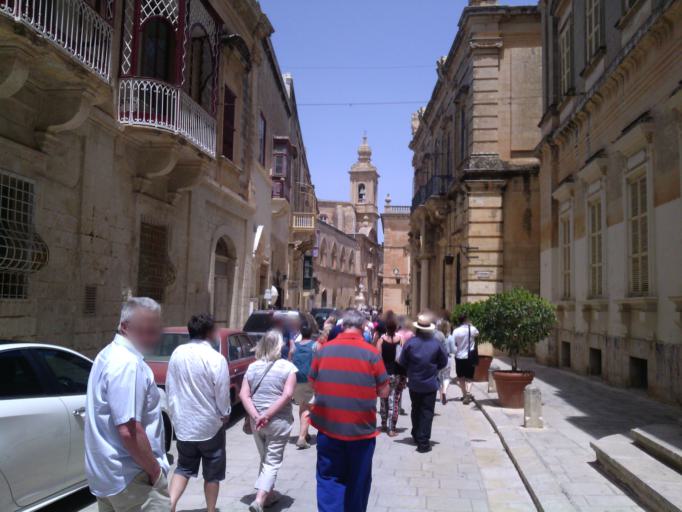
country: MT
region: L-Imdina
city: Imdina
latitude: 35.8857
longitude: 14.4034
